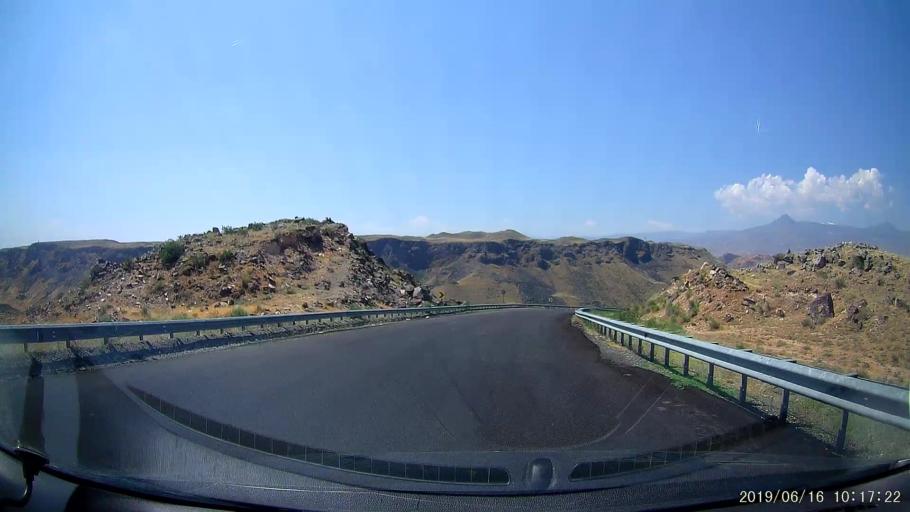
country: TR
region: Igdir
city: Tuzluca
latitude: 40.1684
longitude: 43.6823
